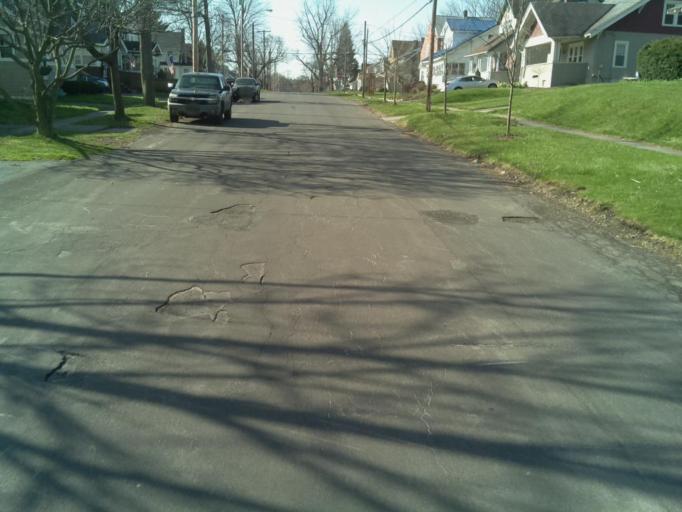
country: US
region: New York
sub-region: Onondaga County
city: Lyncourt
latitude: 43.0648
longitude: -76.1058
